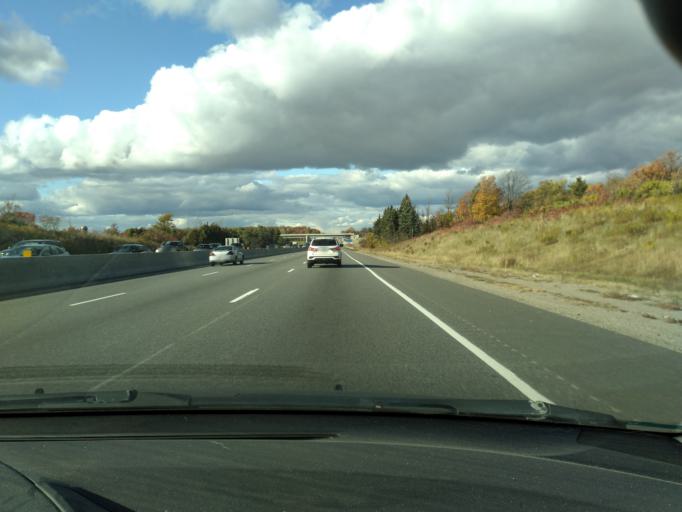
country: CA
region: Ontario
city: Innisfil
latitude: 44.2568
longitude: -79.6719
